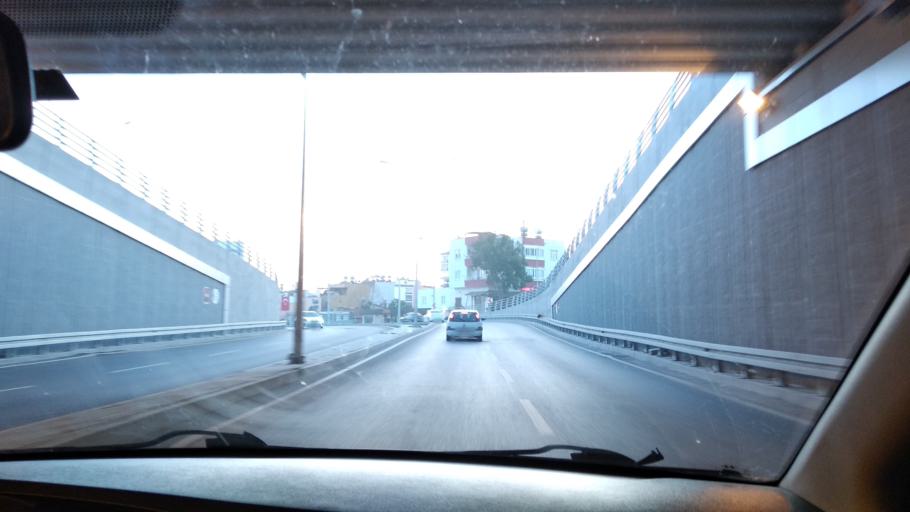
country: TR
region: Mersin
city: Mercin
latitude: 36.8200
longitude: 34.5973
